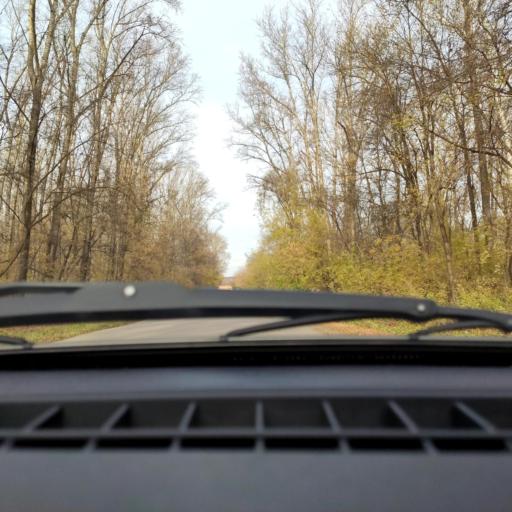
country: RU
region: Bashkortostan
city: Ufa
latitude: 54.7938
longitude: 56.1550
